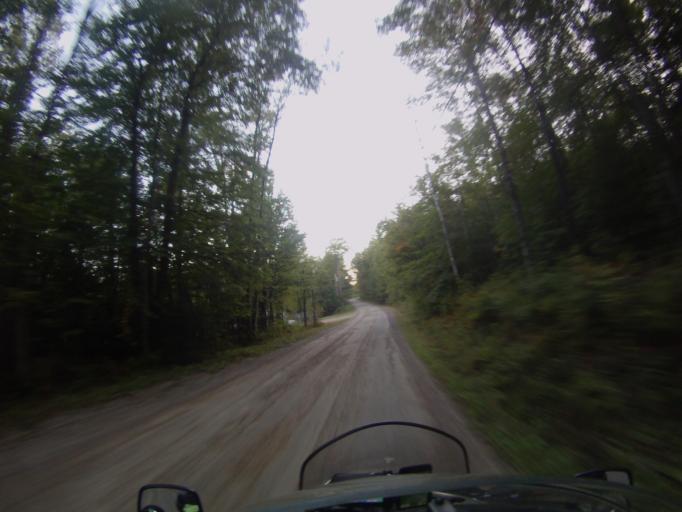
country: US
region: Vermont
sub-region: Addison County
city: Middlebury (village)
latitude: 44.0053
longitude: -73.0367
